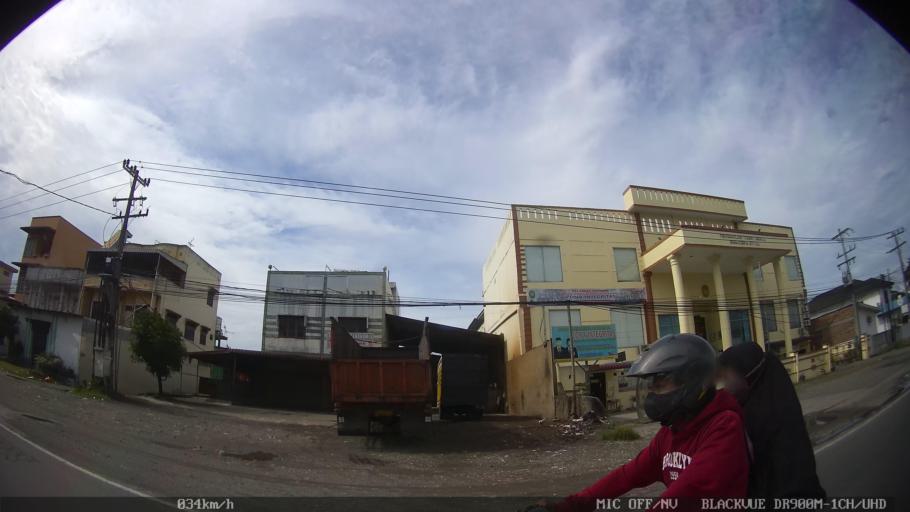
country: ID
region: North Sumatra
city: Medan
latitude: 3.6153
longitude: 98.6470
